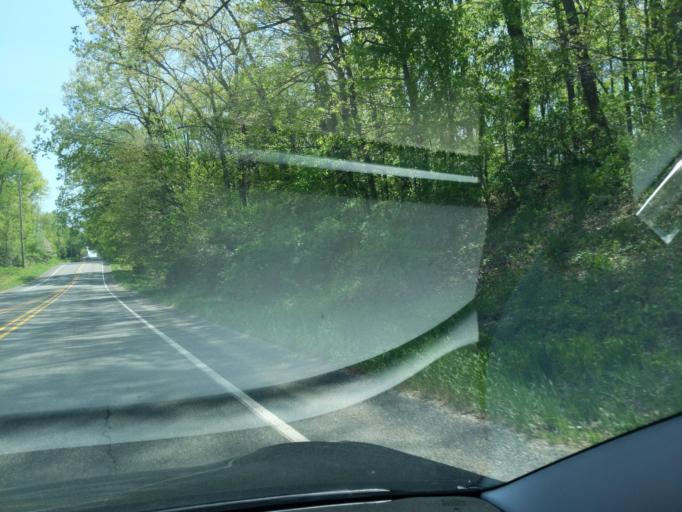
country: US
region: Michigan
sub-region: Kent County
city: Forest Hills
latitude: 42.9549
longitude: -85.5403
